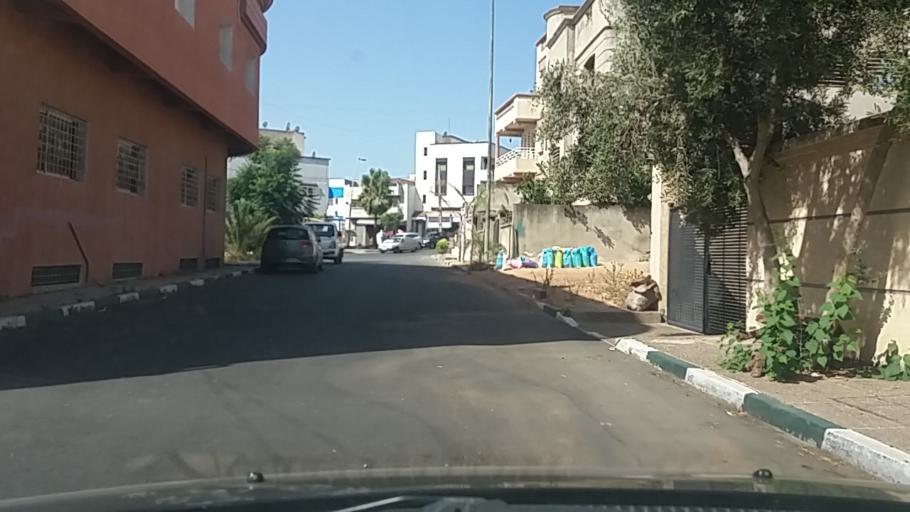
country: MA
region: Gharb-Chrarda-Beni Hssen
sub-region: Kenitra Province
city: Kenitra
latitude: 34.2661
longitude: -6.6128
